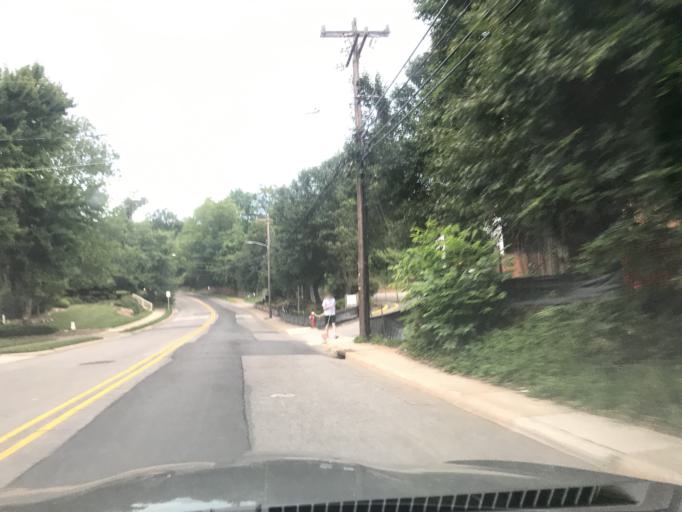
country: US
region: North Carolina
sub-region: Orange County
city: Chapel Hill
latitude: 35.9208
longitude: -79.0518
